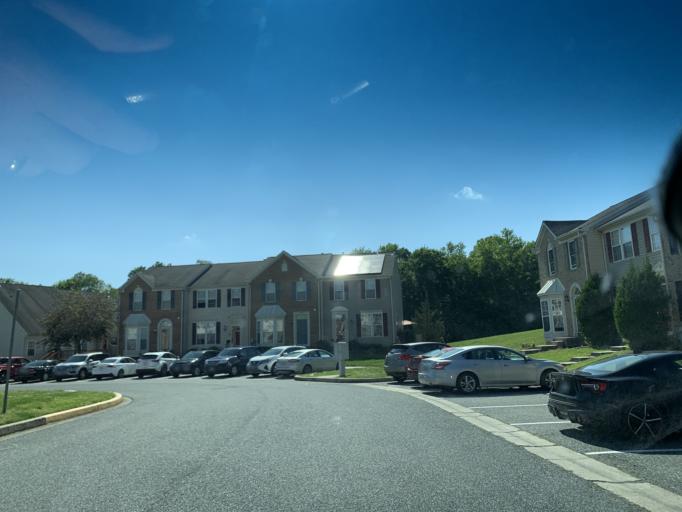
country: US
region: Maryland
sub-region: Harford County
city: Perryman
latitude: 39.4949
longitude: -76.2163
